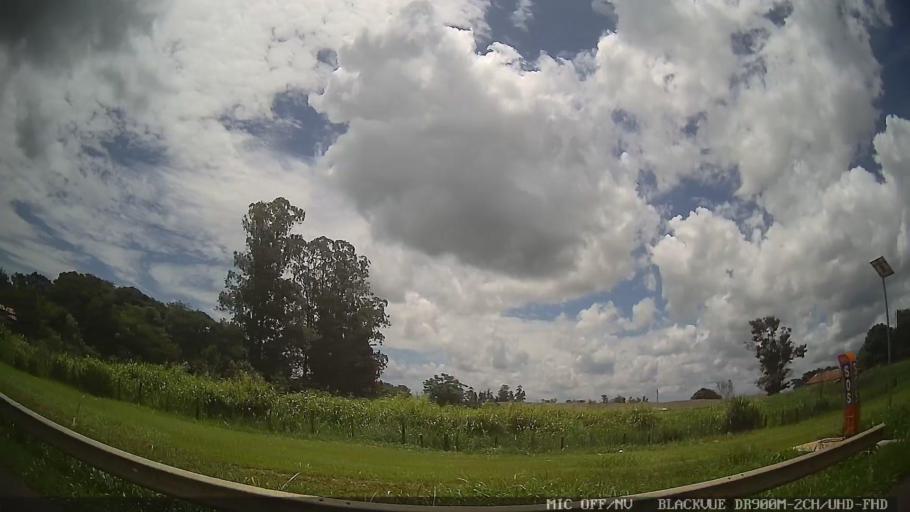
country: BR
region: Sao Paulo
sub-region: Laranjal Paulista
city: Laranjal Paulista
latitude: -23.0407
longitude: -47.9029
